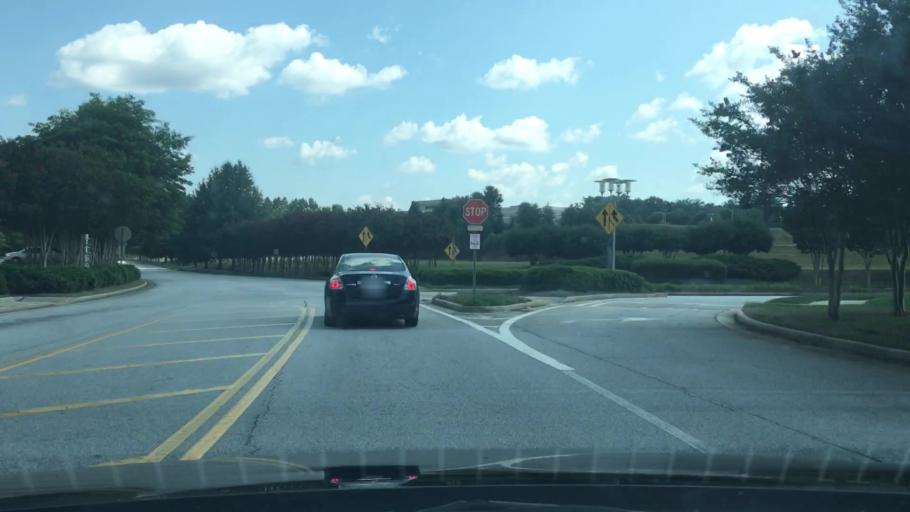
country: US
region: Georgia
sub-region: DeKalb County
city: Lithonia
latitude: 33.6986
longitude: -84.0993
